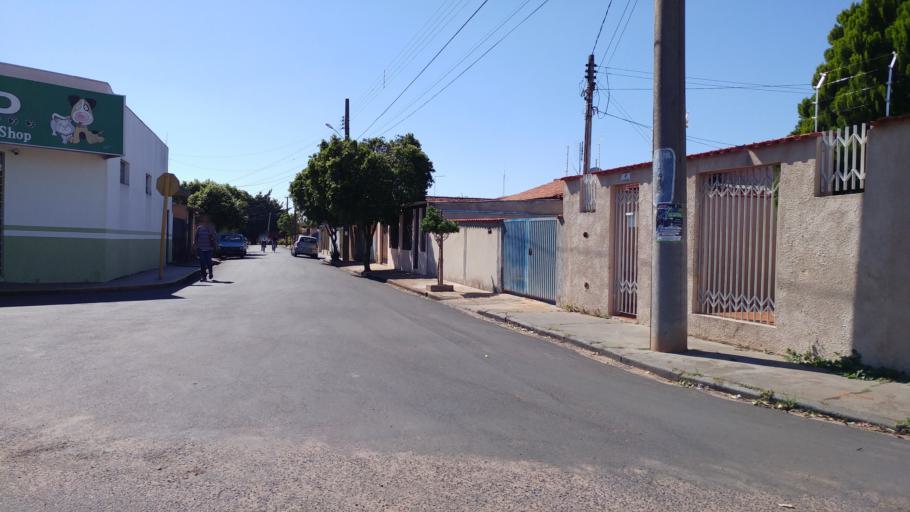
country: BR
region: Sao Paulo
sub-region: Paraguacu Paulista
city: Paraguacu Paulista
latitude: -22.4277
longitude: -50.5822
